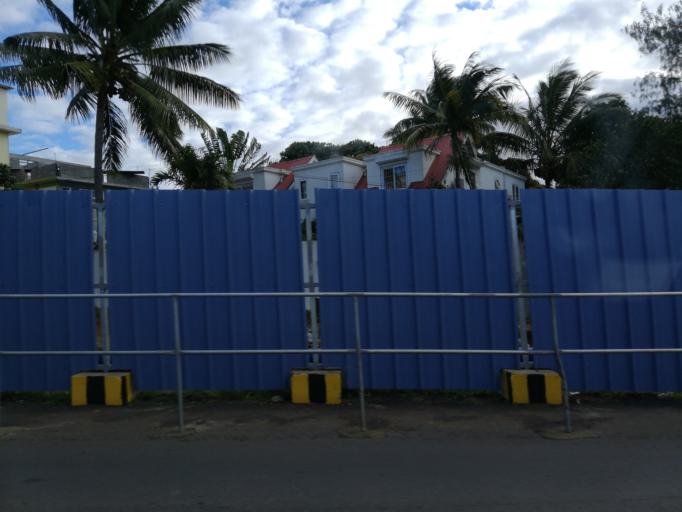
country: MU
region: Plaines Wilhems
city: Ebene
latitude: -20.2311
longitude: 57.4708
